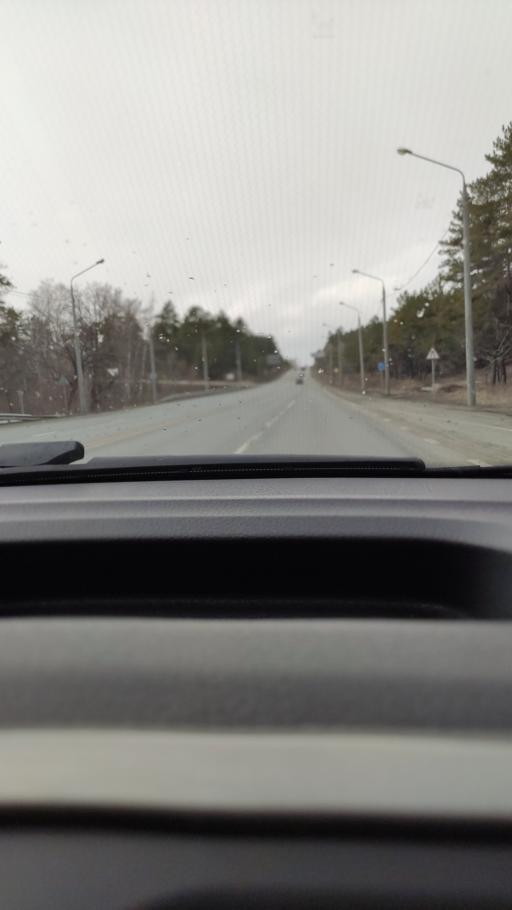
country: RU
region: Samara
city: Volzhskiy
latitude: 53.4391
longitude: 50.1092
